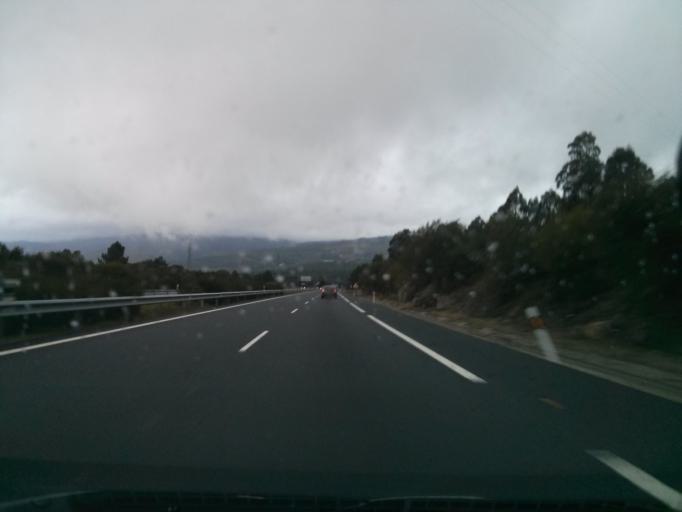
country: ES
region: Galicia
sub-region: Provincia de Ourense
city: Melon
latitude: 42.2049
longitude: -8.2698
